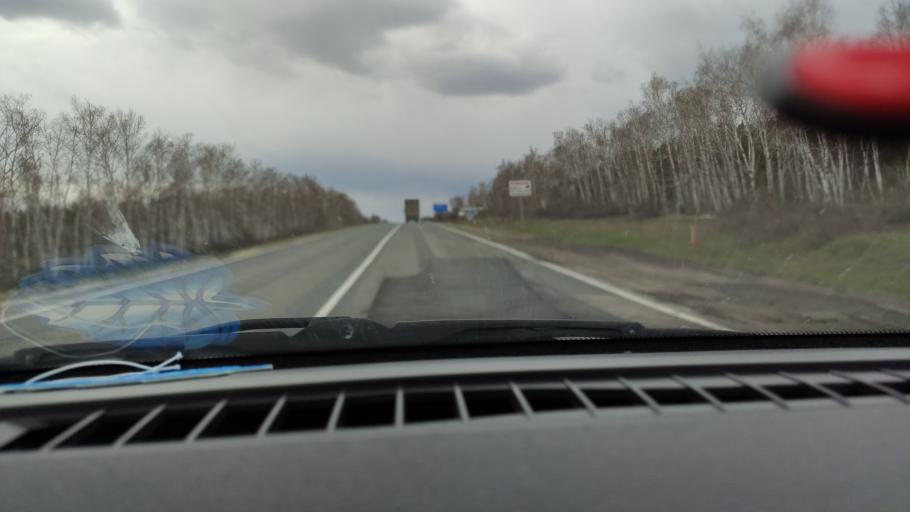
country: RU
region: Saratov
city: Sennoy
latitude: 52.1164
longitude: 46.8385
